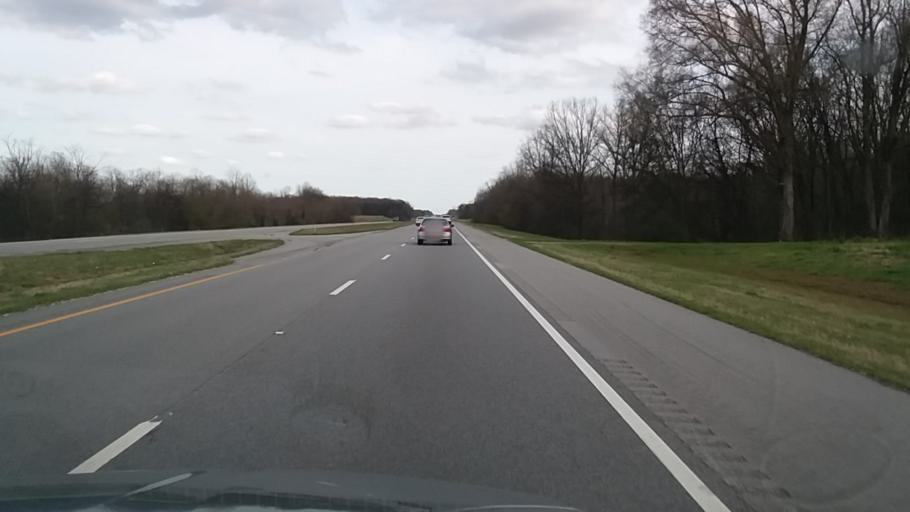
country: US
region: Alabama
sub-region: Lawrence County
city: Town Creek
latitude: 34.6831
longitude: -87.4944
